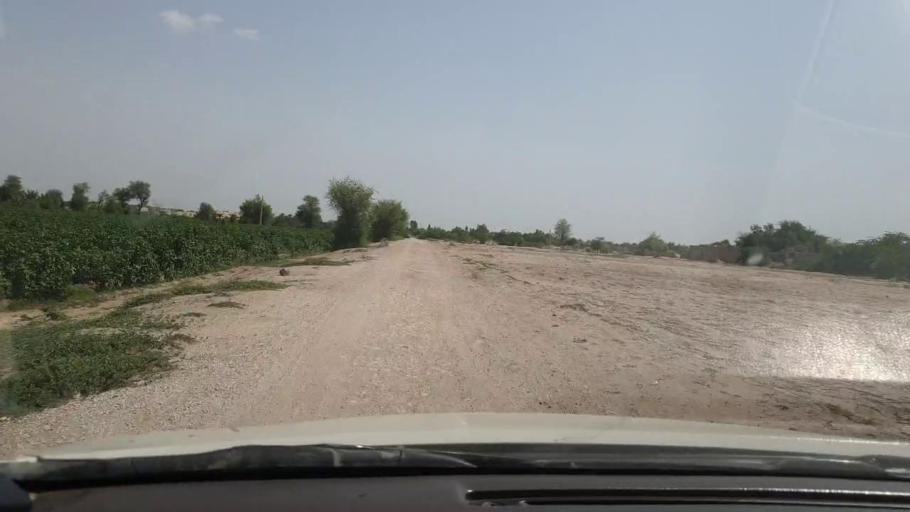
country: PK
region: Sindh
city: Rohri
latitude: 27.4681
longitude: 69.0789
